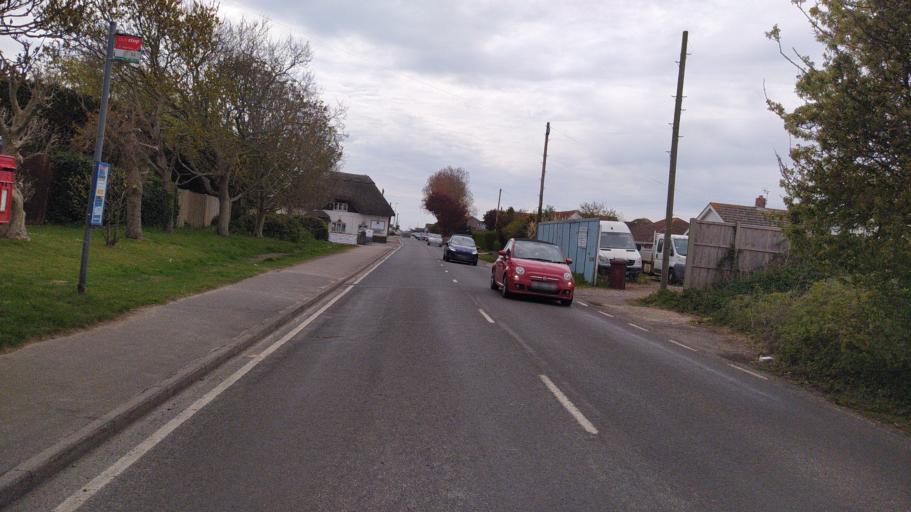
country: GB
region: England
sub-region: West Sussex
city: East Wittering
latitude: 50.7669
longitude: -0.8561
